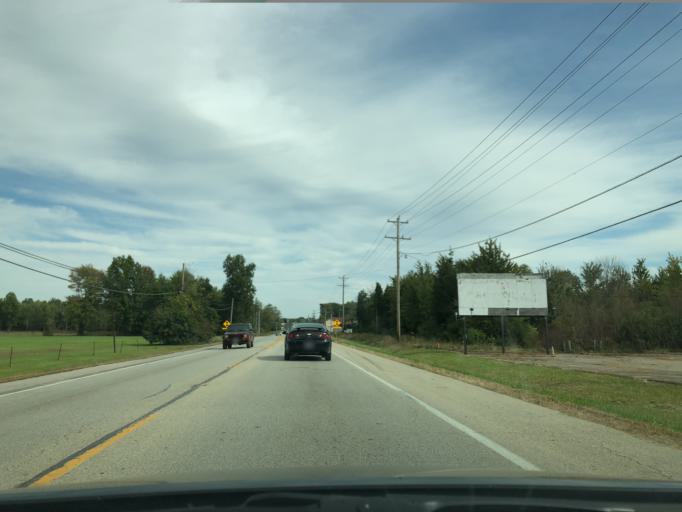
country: US
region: Ohio
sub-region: Clermont County
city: Mount Repose
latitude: 39.2178
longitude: -84.1956
